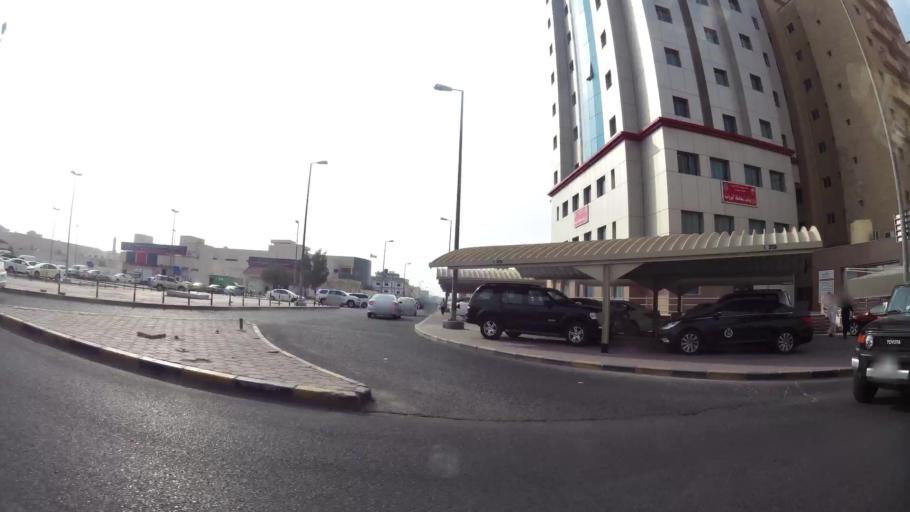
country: KW
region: Al Farwaniyah
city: Al Farwaniyah
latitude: 29.2873
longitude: 47.9552
